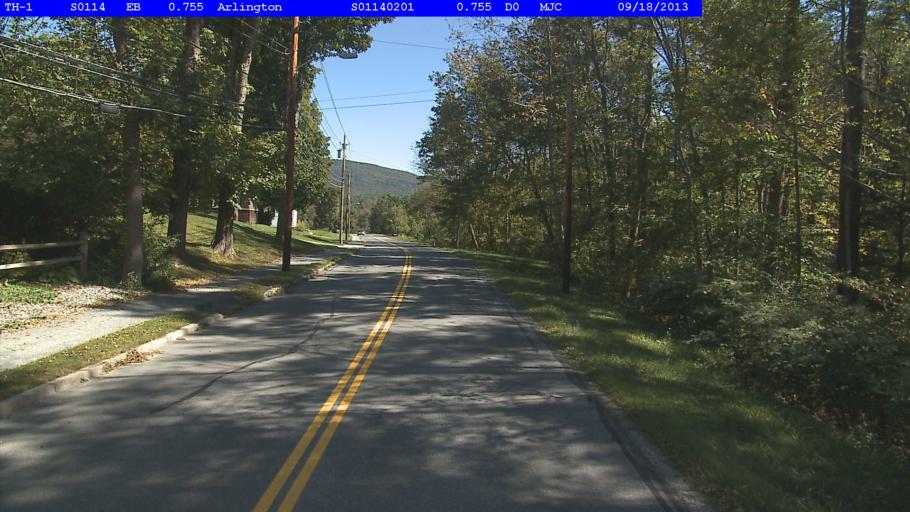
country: US
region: Vermont
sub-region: Bennington County
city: Arlington
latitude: 43.0632
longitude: -73.1496
